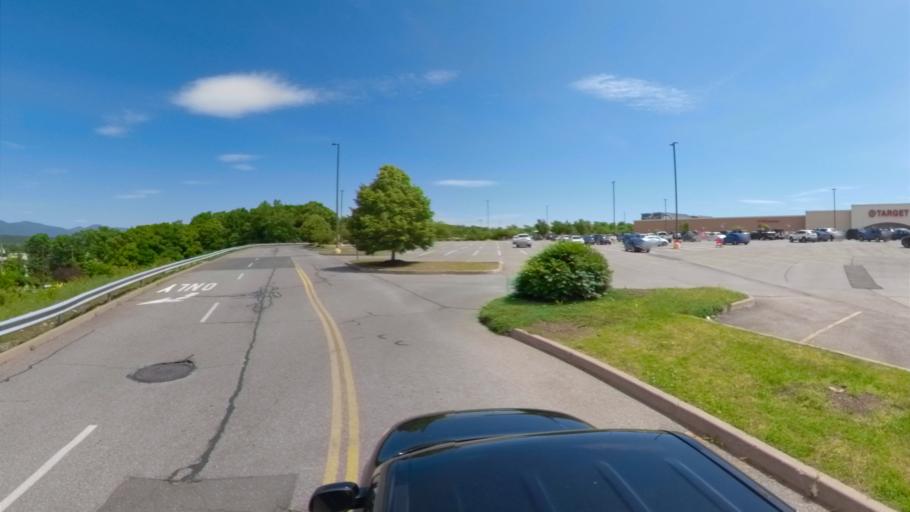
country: US
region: New York
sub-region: Ulster County
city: Lake Katrine
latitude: 41.9686
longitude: -73.9872
